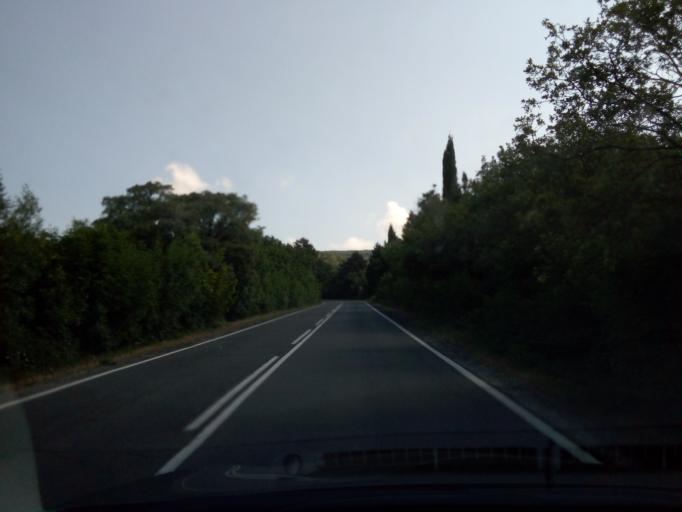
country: BG
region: Burgas
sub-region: Obshtina Nesebur
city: Sveti Vlas
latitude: 42.7213
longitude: 27.7278
